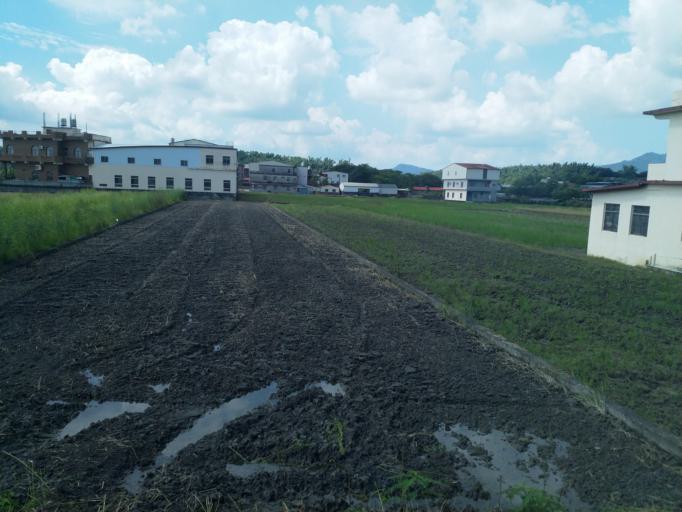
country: TW
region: Taiwan
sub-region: Pingtung
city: Pingtung
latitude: 22.8761
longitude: 120.5744
